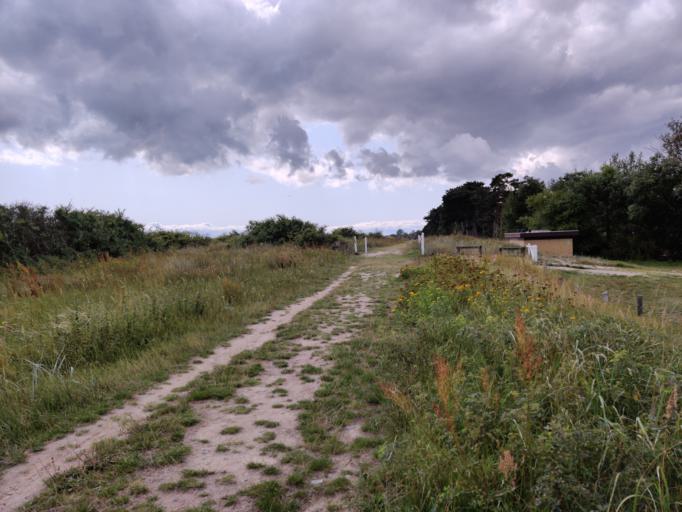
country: DK
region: Zealand
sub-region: Guldborgsund Kommune
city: Nykobing Falster
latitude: 54.7136
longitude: 11.9959
